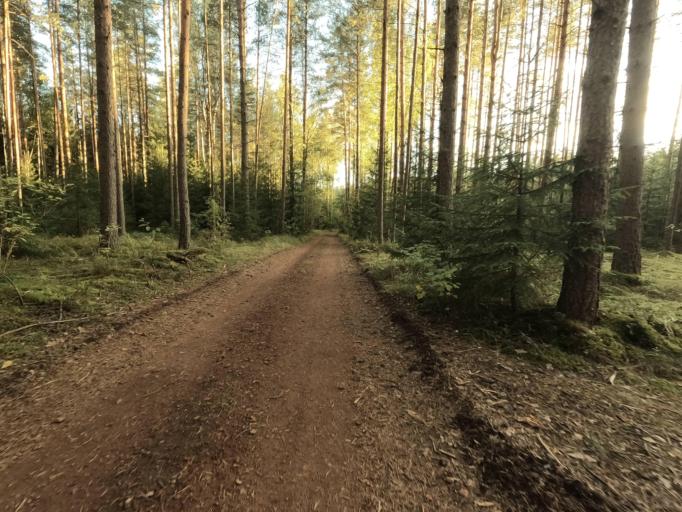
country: RU
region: Leningrad
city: Otradnoye
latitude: 59.8379
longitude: 30.7716
